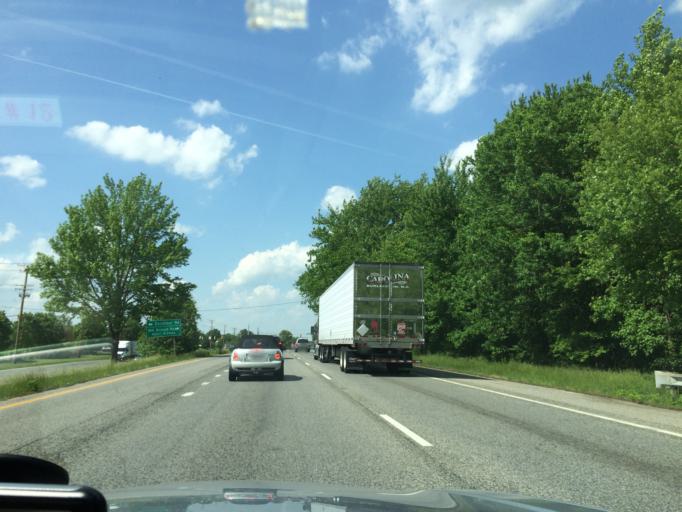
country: US
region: Maryland
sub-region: Prince George's County
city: Bowie
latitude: 38.9332
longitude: -76.7173
